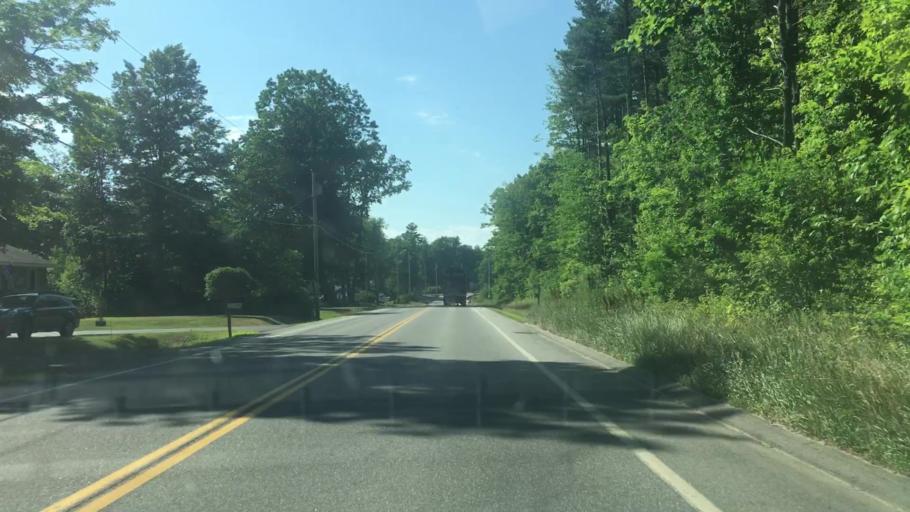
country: US
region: Maine
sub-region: York County
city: Buxton
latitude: 43.5897
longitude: -70.5223
